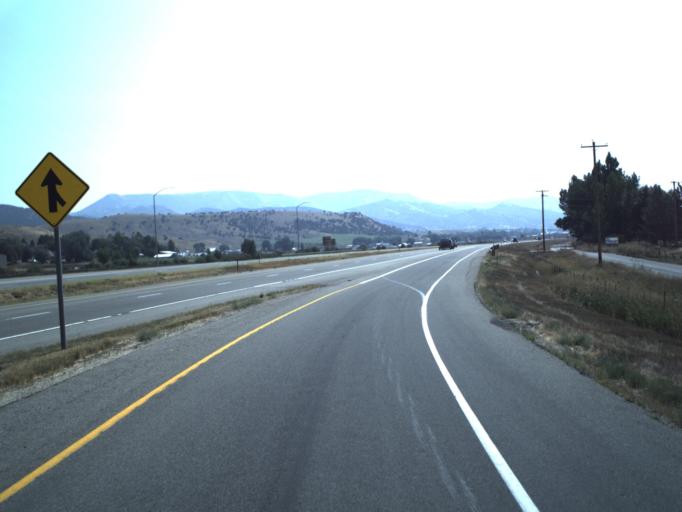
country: US
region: Utah
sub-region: Summit County
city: Coalville
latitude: 40.9101
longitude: -111.4013
